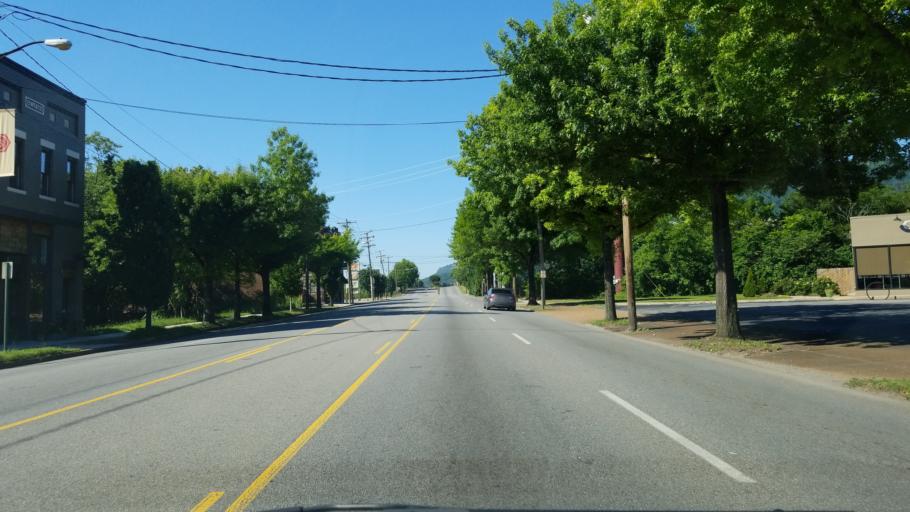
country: US
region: Tennessee
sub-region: Hamilton County
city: Chattanooga
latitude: 35.0268
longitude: -85.3173
